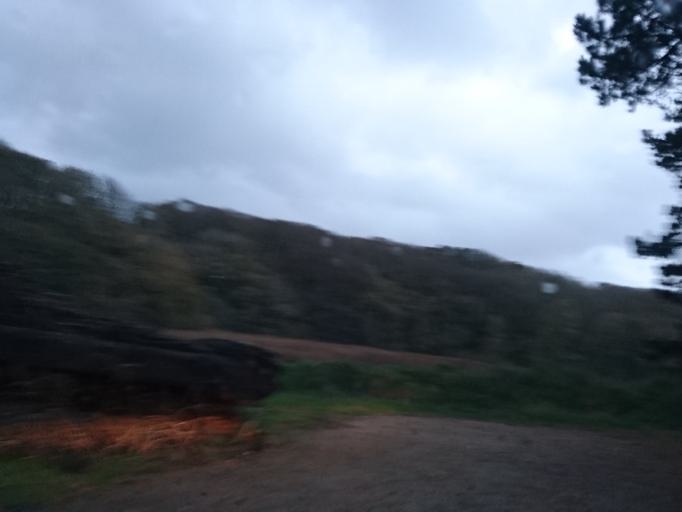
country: FR
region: Brittany
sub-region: Departement du Finistere
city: Le Conquet
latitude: 48.3667
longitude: -4.7469
